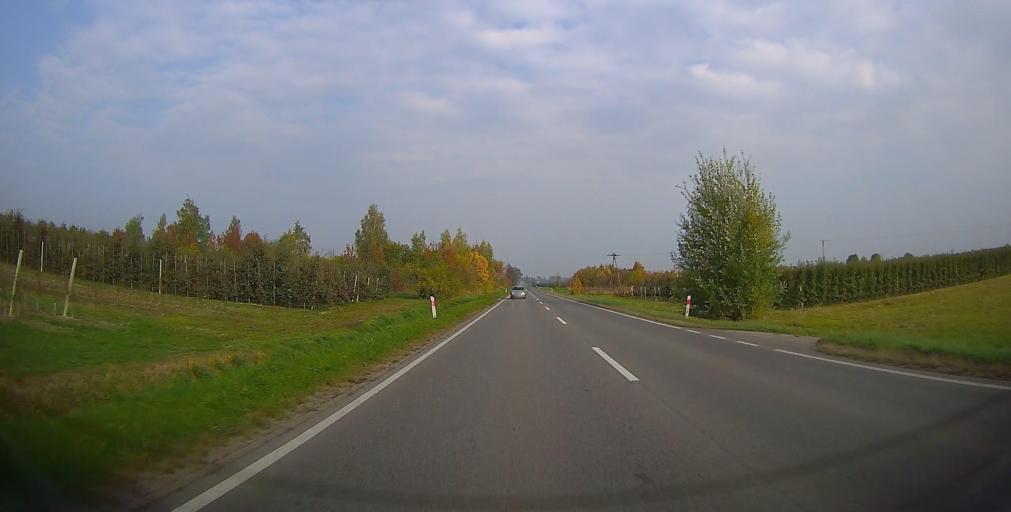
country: PL
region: Masovian Voivodeship
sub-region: Powiat grojecki
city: Bledow
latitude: 51.7575
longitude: 20.7658
